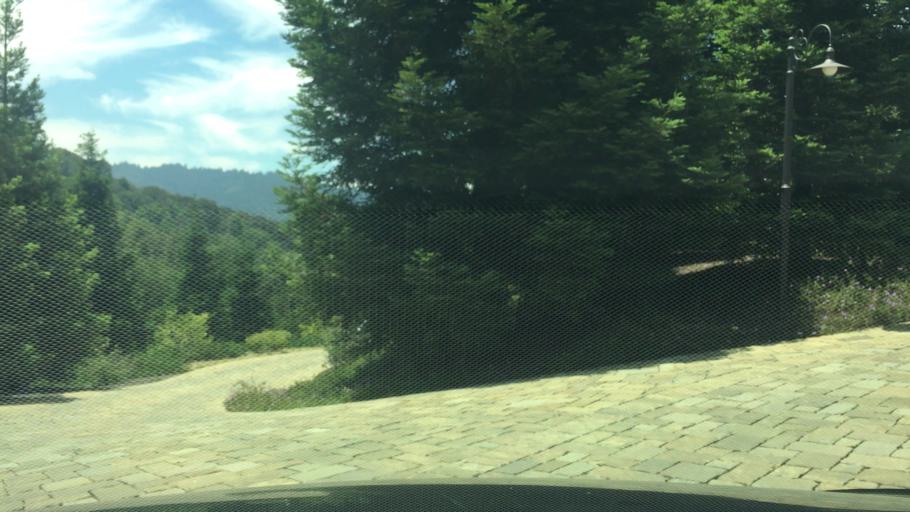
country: US
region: California
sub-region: San Mateo County
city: Ladera
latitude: 37.3687
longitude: -122.1761
